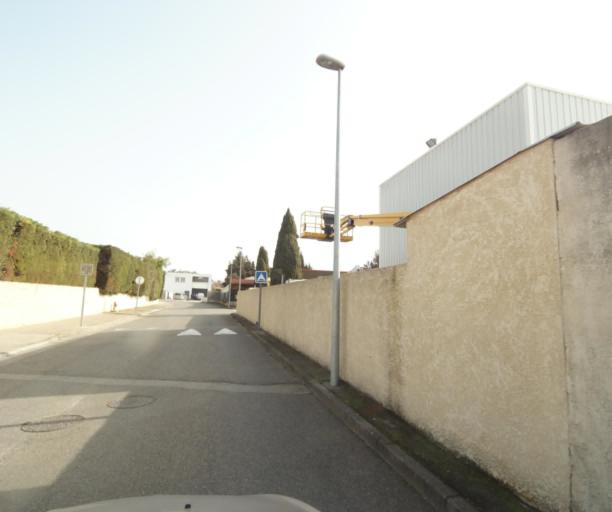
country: FR
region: Provence-Alpes-Cote d'Azur
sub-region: Departement des Bouches-du-Rhone
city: Les Pennes-Mirabeau
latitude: 43.4186
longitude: 5.2962
